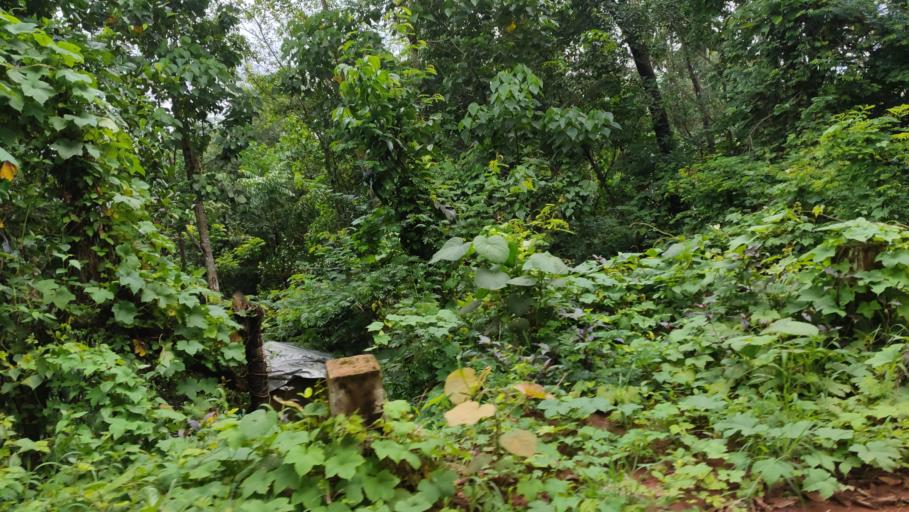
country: IN
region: Kerala
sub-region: Kasaragod District
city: Nileshwar
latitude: 12.2968
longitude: 75.2878
